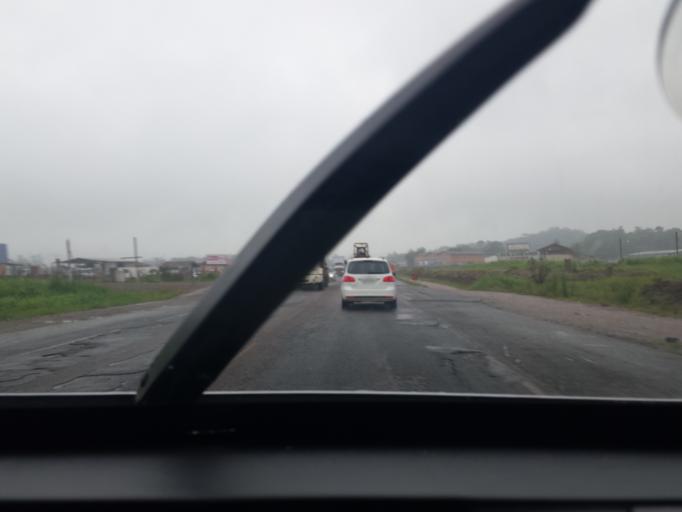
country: BR
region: Santa Catarina
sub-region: Navegantes
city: Navegantes
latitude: -26.8332
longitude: -48.7299
